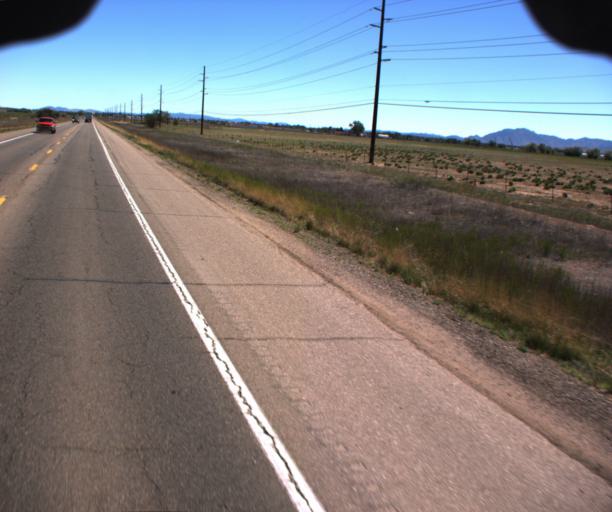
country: US
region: Arizona
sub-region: Yavapai County
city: Chino Valley
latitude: 34.8192
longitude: -112.4548
